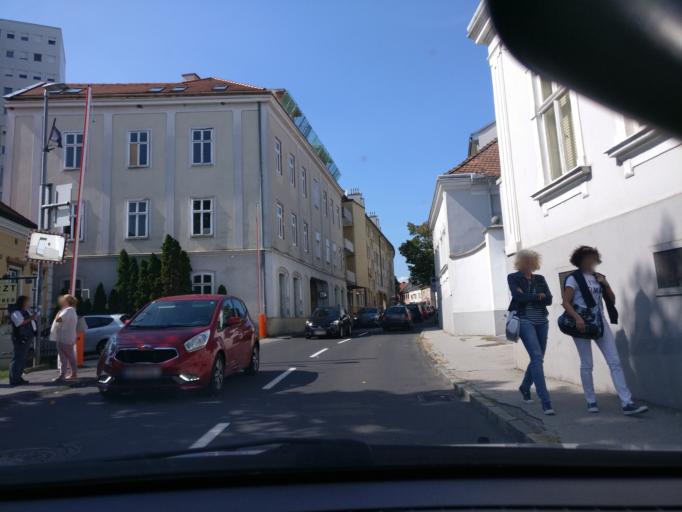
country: AT
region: Burgenland
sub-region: Politischer Bezirk Mattersburg
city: Mattersburg
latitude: 47.7391
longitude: 16.4011
